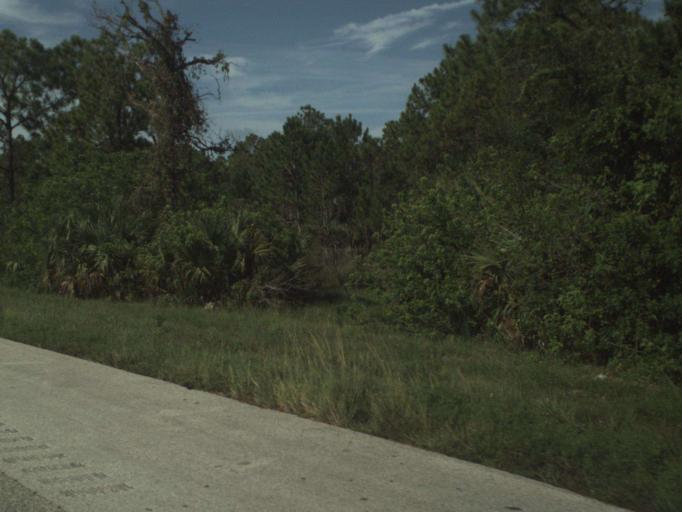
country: US
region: Florida
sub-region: Indian River County
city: Fellsmere
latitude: 27.8046
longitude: -80.5492
